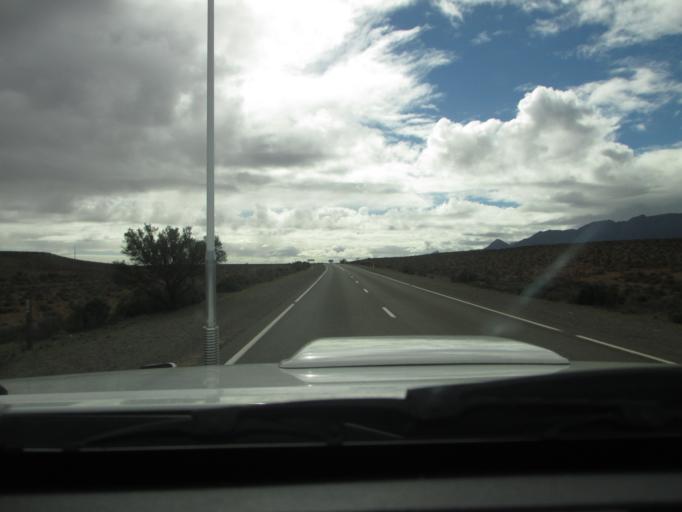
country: AU
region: South Australia
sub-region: Flinders Ranges
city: Quorn
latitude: -31.5667
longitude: 138.4270
